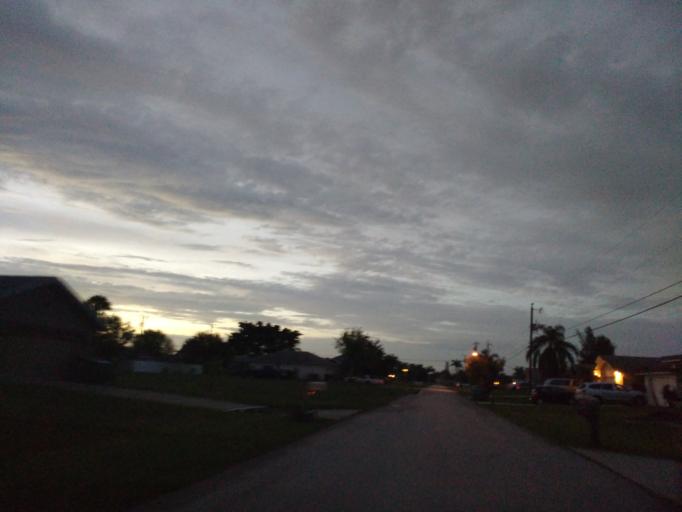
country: US
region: Florida
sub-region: Lee County
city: Cape Coral
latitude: 26.6170
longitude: -81.9629
